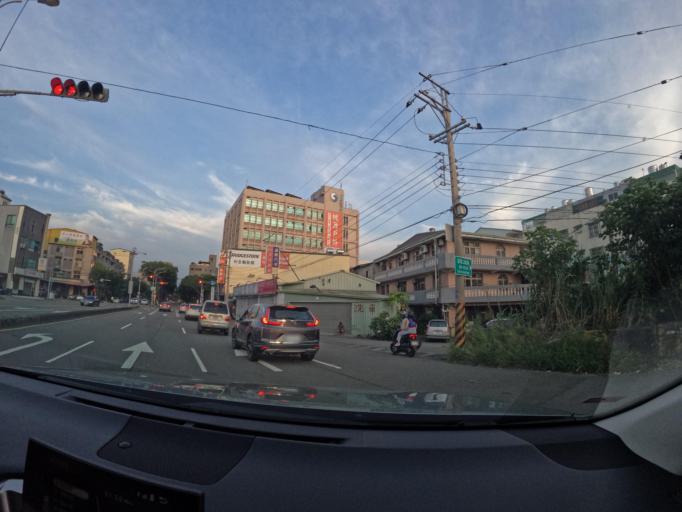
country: TW
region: Taiwan
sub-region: Taichung City
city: Taichung
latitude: 24.1191
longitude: 120.6843
